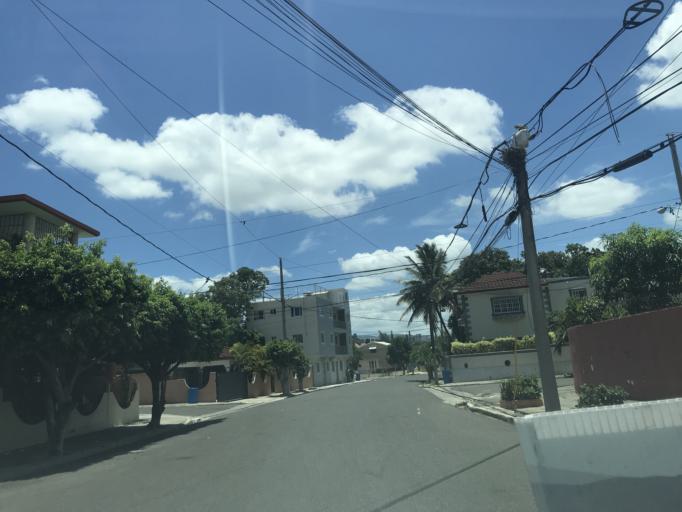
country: DO
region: Santiago
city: Santiago de los Caballeros
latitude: 19.4391
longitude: -70.6959
